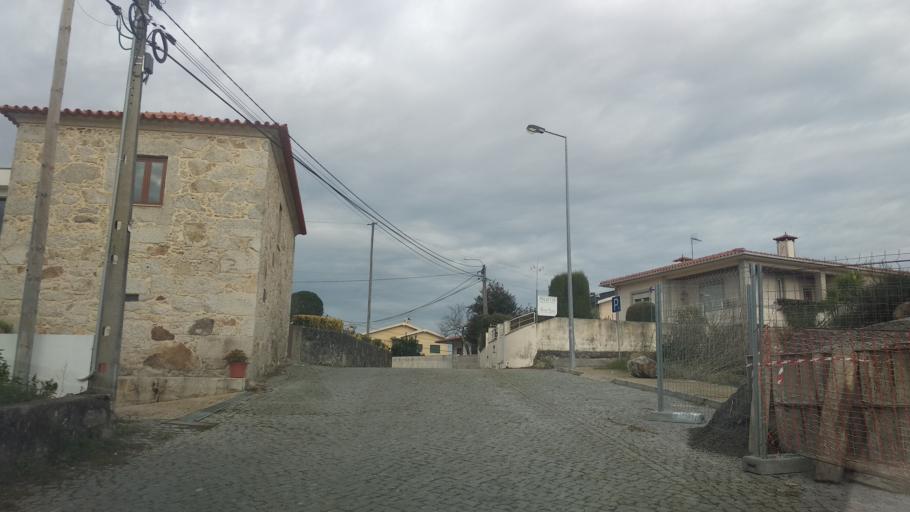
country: PT
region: Braga
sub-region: Braga
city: Braga
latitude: 41.5434
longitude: -8.4605
